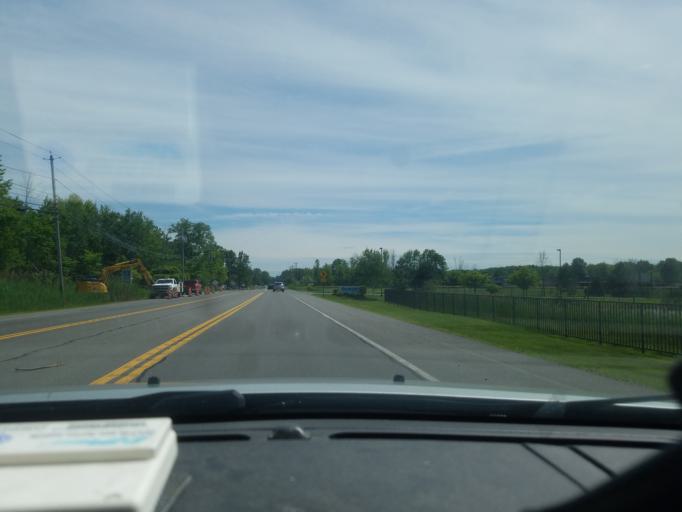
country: US
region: New York
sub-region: Onondaga County
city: East Syracuse
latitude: 43.0824
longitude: -76.0586
